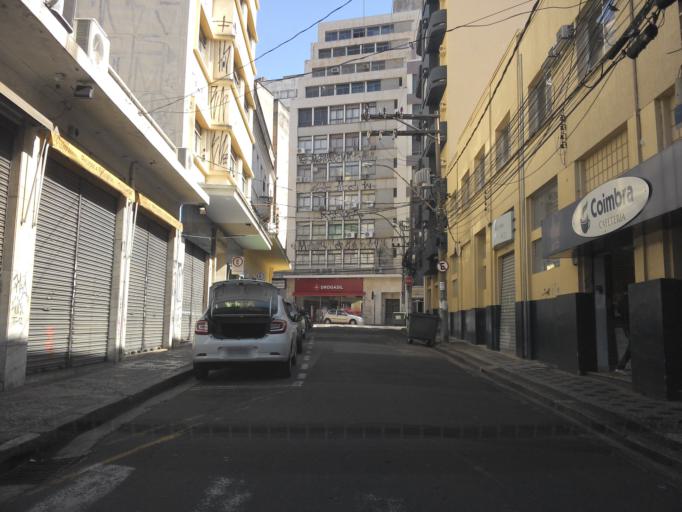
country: BR
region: Sao Paulo
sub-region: Campinas
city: Campinas
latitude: -22.9044
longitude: -47.0585
